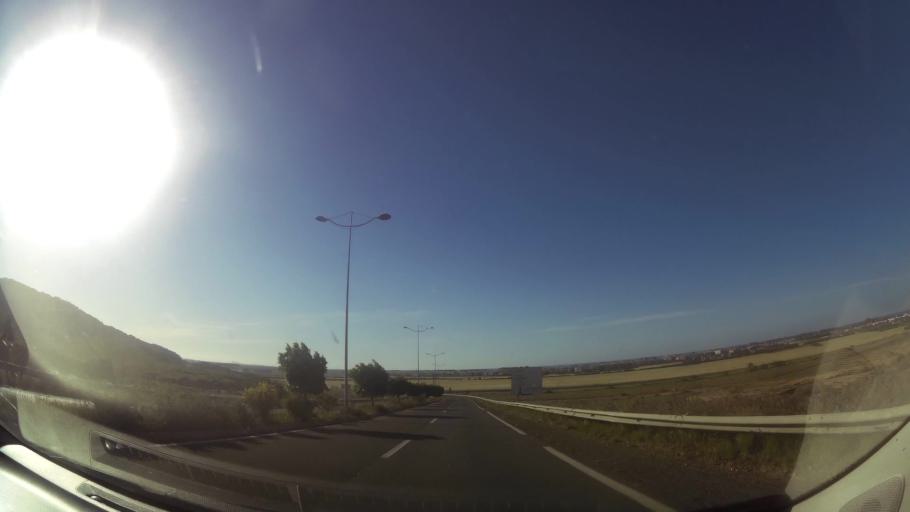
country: MA
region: Oriental
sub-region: Berkane-Taourirt
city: Madagh
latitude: 35.0615
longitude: -2.2239
